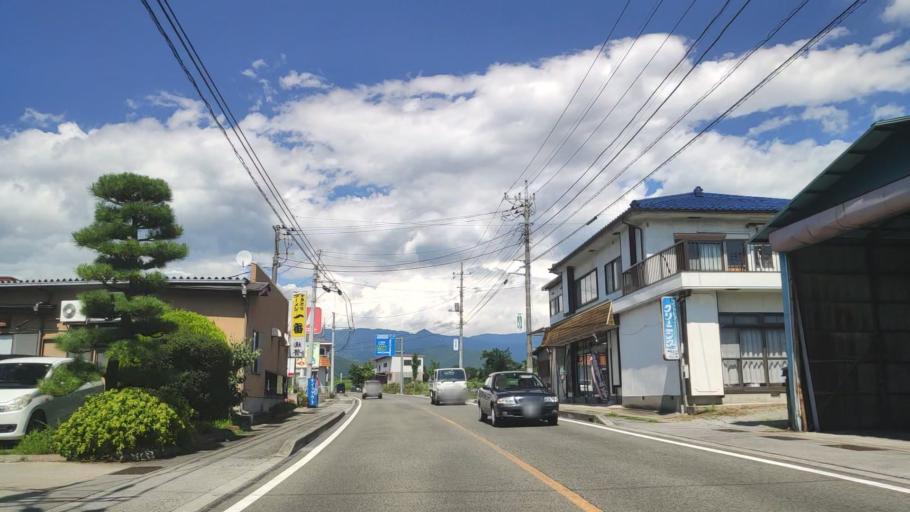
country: JP
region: Yamanashi
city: Enzan
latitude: 35.7002
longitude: 138.6896
